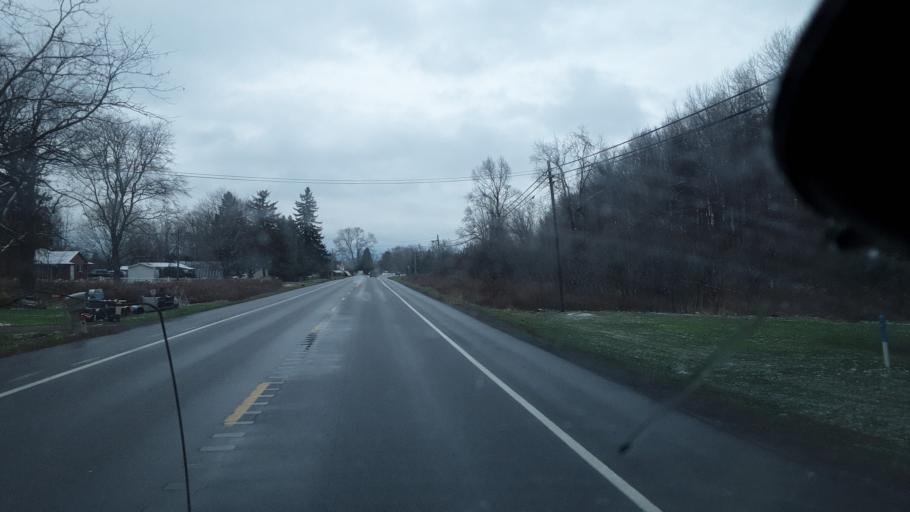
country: US
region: New York
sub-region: Cattaraugus County
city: Delevan
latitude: 42.4647
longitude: -78.4822
